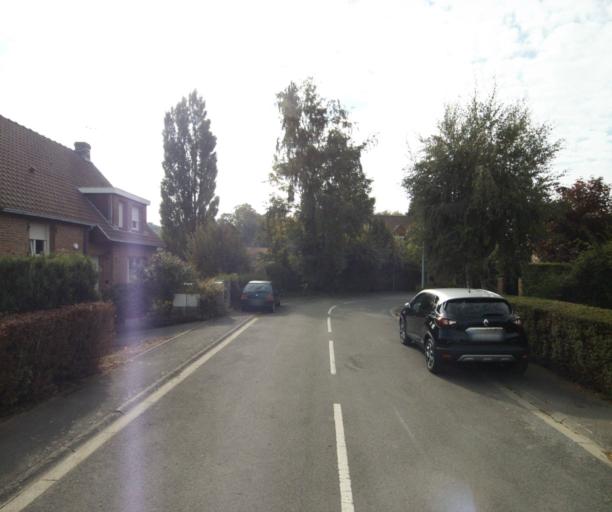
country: FR
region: Nord-Pas-de-Calais
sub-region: Departement du Nord
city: Wattignies
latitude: 50.5814
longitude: 3.0343
